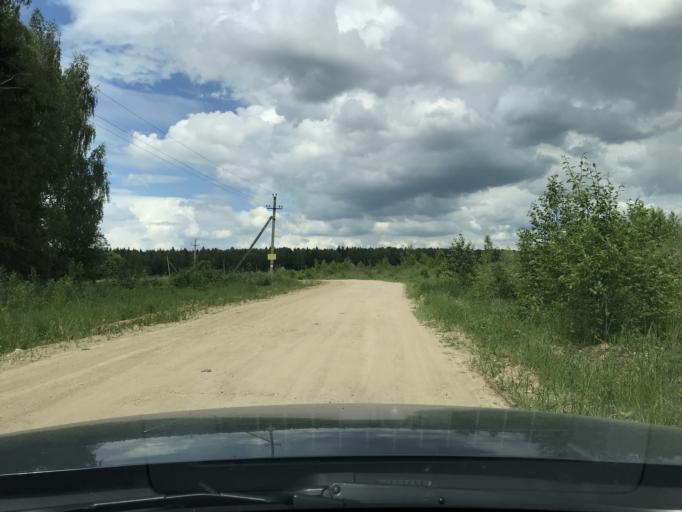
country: RU
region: Moskovskaya
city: Vereya
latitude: 55.3192
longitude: 36.3221
